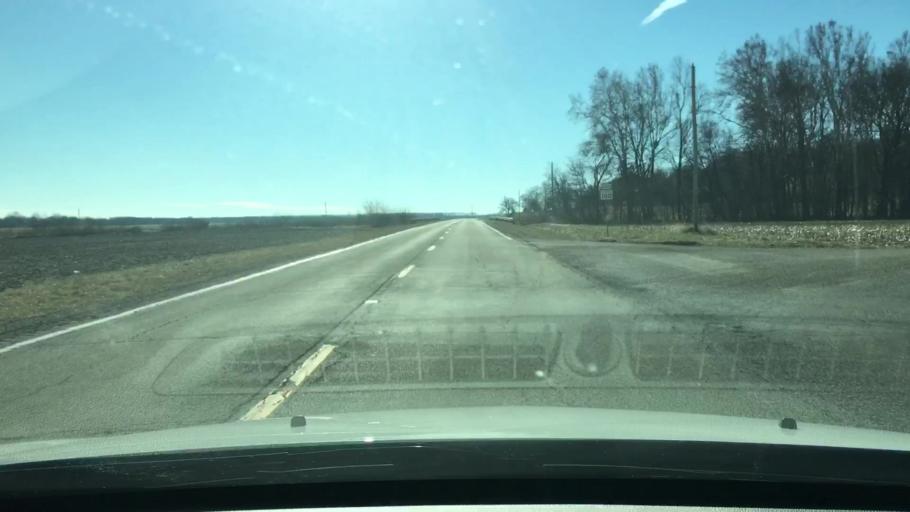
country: US
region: Illinois
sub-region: Mason County
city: Havana
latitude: 40.2634
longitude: -90.1773
